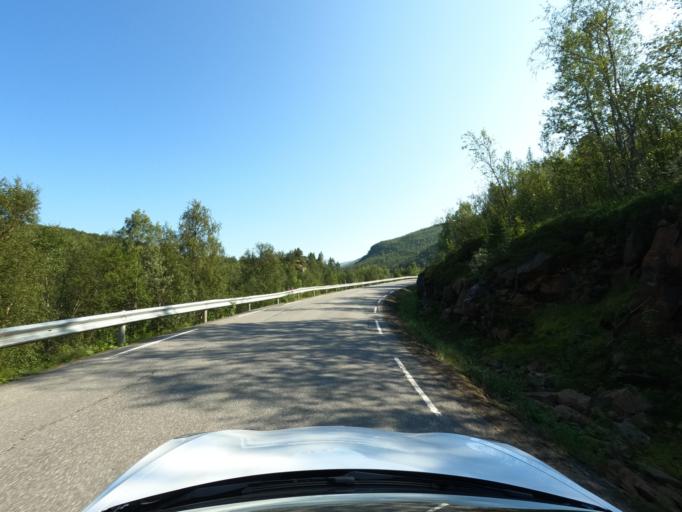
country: NO
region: Nordland
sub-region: Narvik
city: Narvik
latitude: 68.3856
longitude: 17.3463
